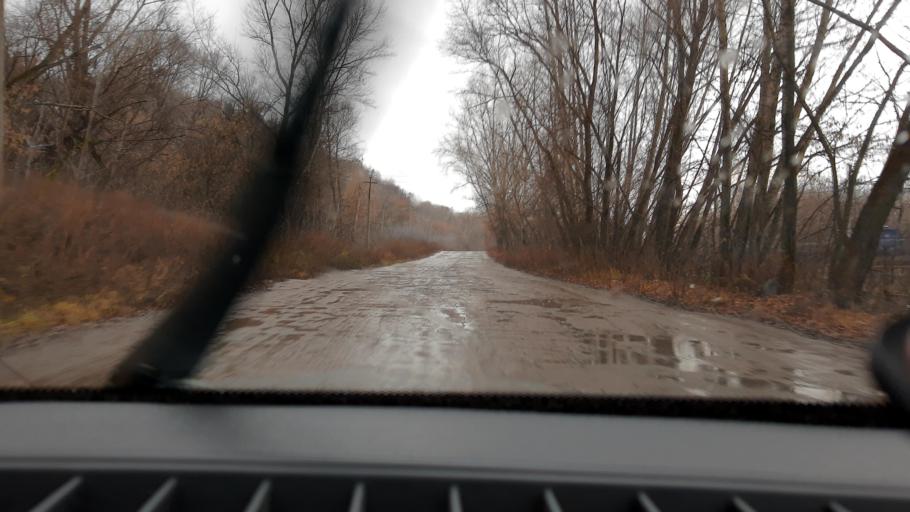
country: RU
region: Bashkortostan
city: Ufa
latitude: 54.7600
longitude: 55.9756
